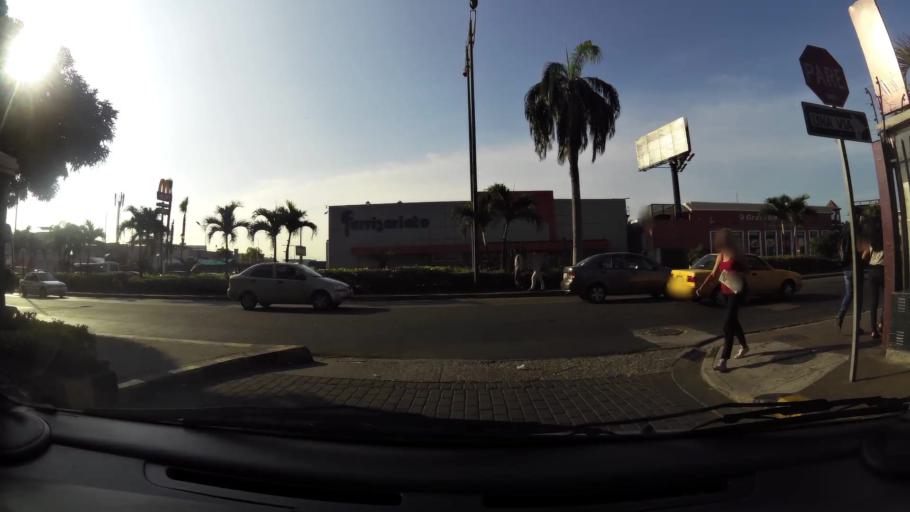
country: EC
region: Guayas
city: Guayaquil
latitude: -2.1684
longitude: -79.8971
